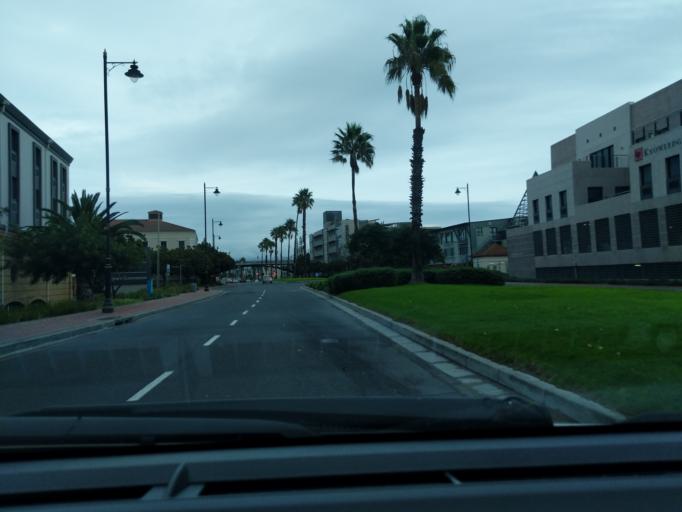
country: ZA
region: Western Cape
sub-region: City of Cape Town
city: Sunset Beach
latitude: -33.8904
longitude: 18.5179
